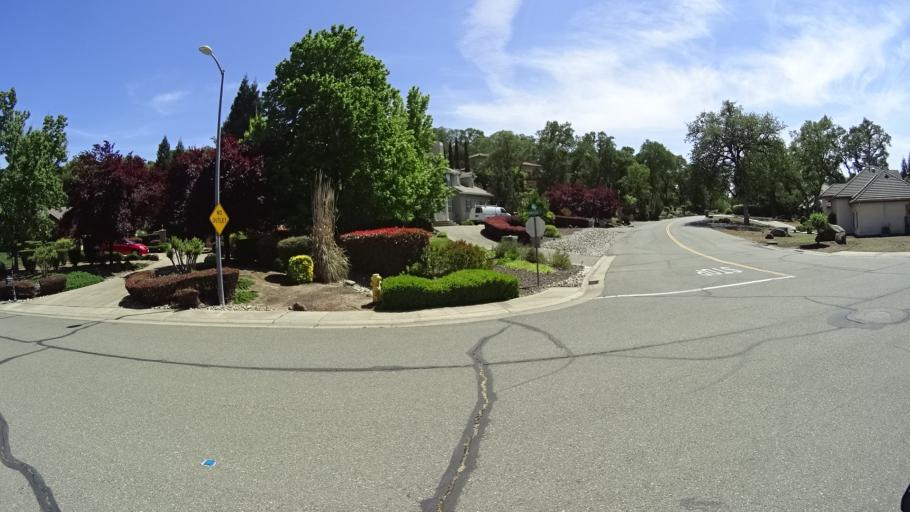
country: US
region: California
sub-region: Placer County
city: Rocklin
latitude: 38.8209
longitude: -121.2307
